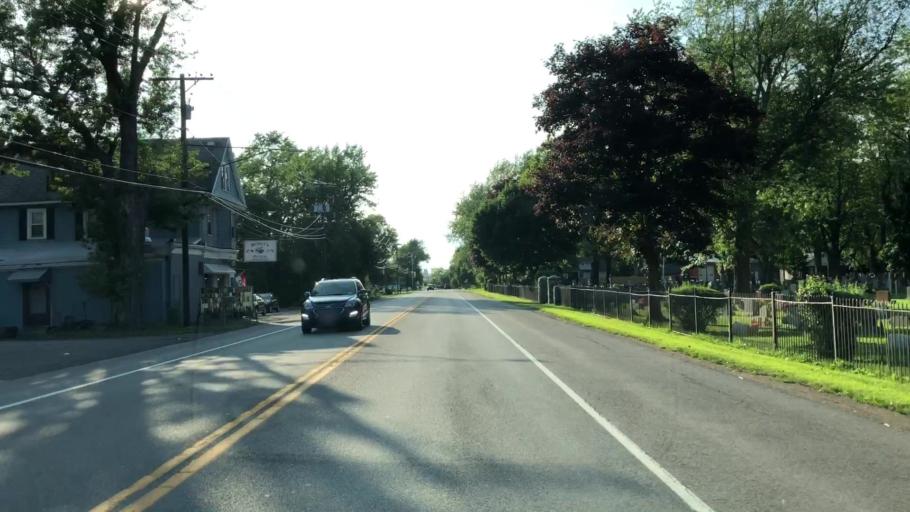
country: US
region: New York
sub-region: Erie County
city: West Seneca
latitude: 42.8688
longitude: -78.7774
